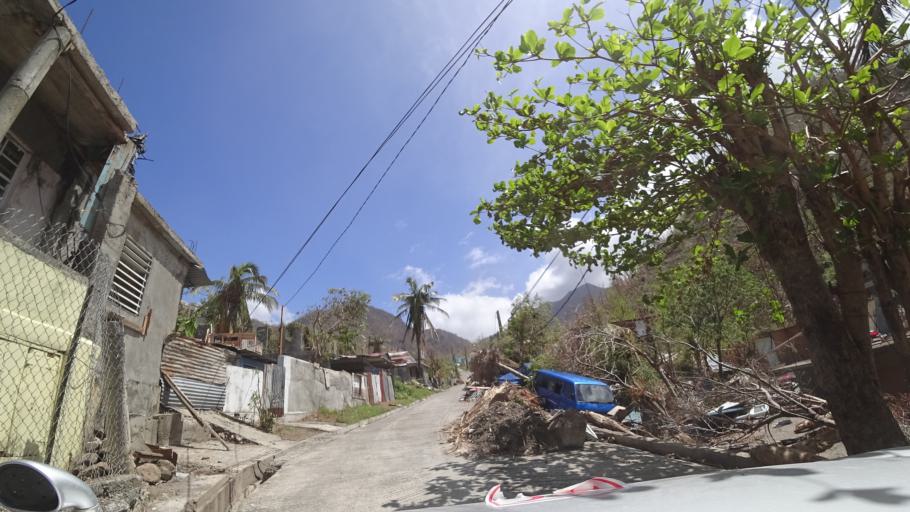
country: DM
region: Saint Luke
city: Pointe Michel
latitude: 15.2593
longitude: -61.3749
